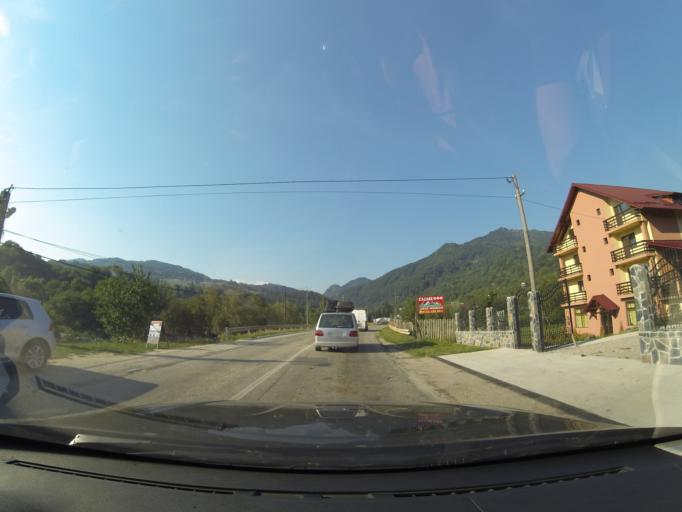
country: RO
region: Arges
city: Poenari
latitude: 45.3327
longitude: 24.6356
